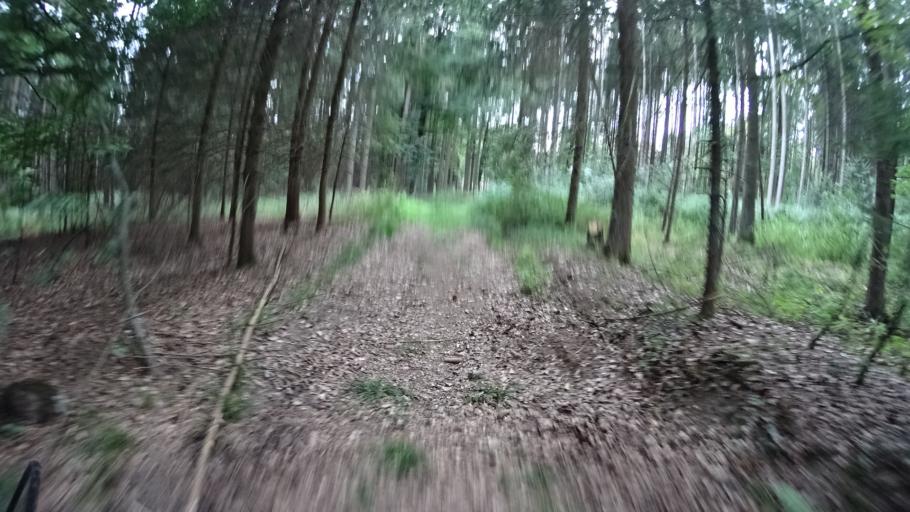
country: DE
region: Bavaria
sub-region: Upper Bavaria
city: Bohmfeld
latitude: 48.8817
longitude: 11.3376
